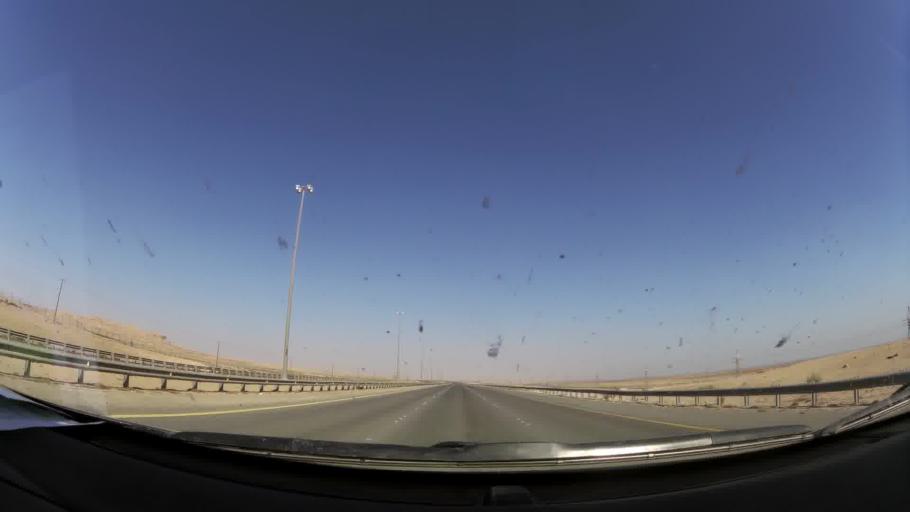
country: KW
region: Muhafazat al Jahra'
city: Al Jahra'
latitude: 29.4898
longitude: 47.7840
